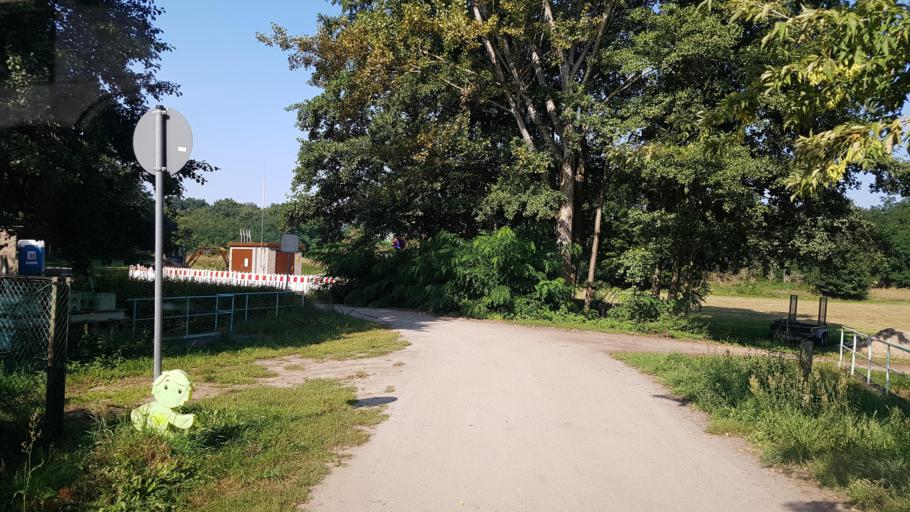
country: DE
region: Brandenburg
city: Vetschau
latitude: 51.7920
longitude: 14.0689
